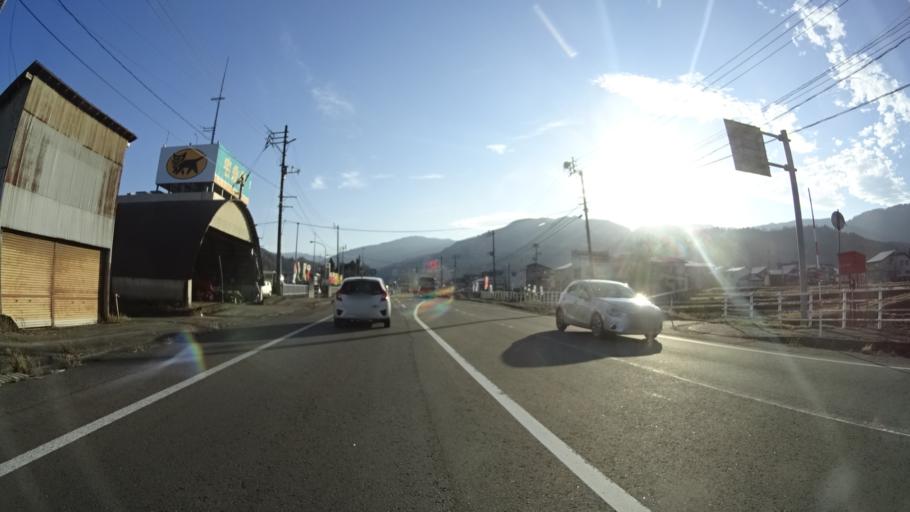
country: JP
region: Niigata
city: Shiozawa
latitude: 36.9869
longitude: 138.8086
